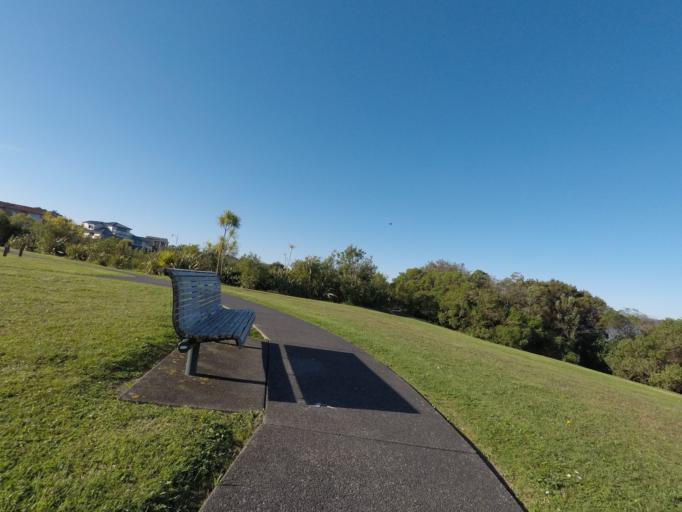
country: NZ
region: Auckland
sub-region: Auckland
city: Rosebank
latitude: -36.8384
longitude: 174.6614
